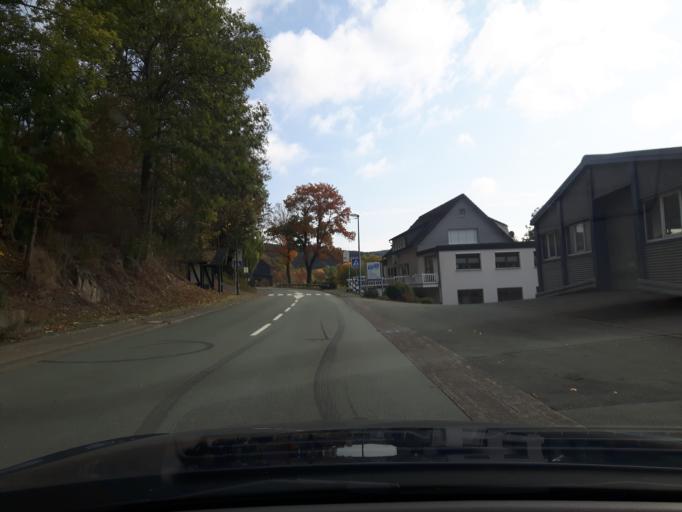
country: DE
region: North Rhine-Westphalia
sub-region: Regierungsbezirk Arnsberg
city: Bad Berleburg
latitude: 51.0136
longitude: 8.4293
